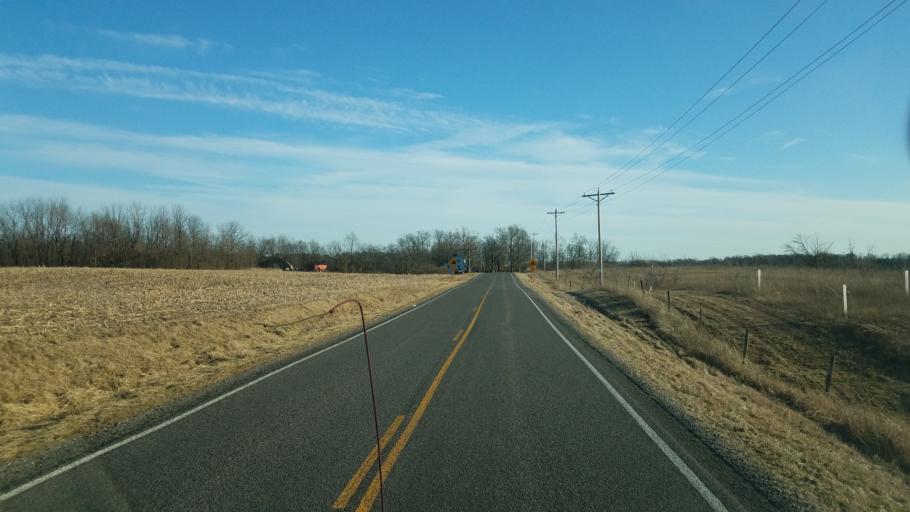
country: US
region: Ohio
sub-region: Logan County
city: West Liberty
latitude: 40.2614
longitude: -83.7190
